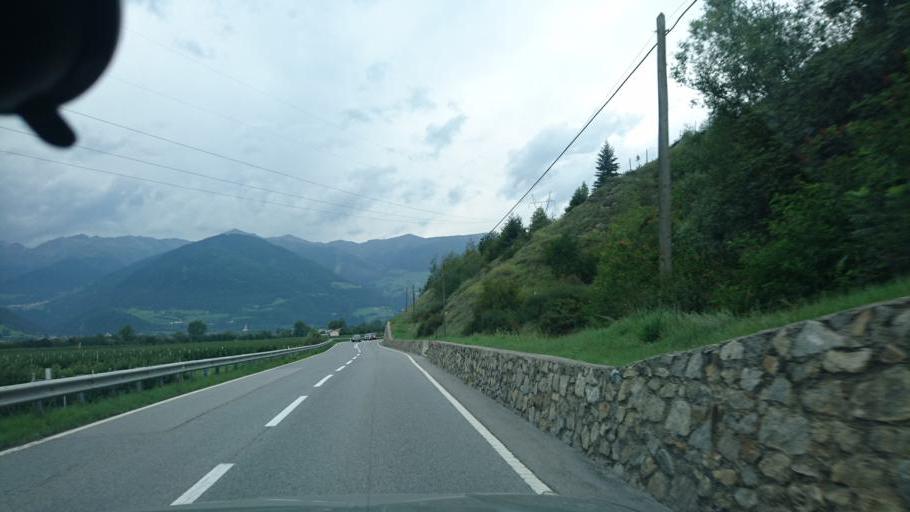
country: IT
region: Trentino-Alto Adige
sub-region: Bolzano
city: Prato Allo Stelvio
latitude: 46.6309
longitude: 10.6316
